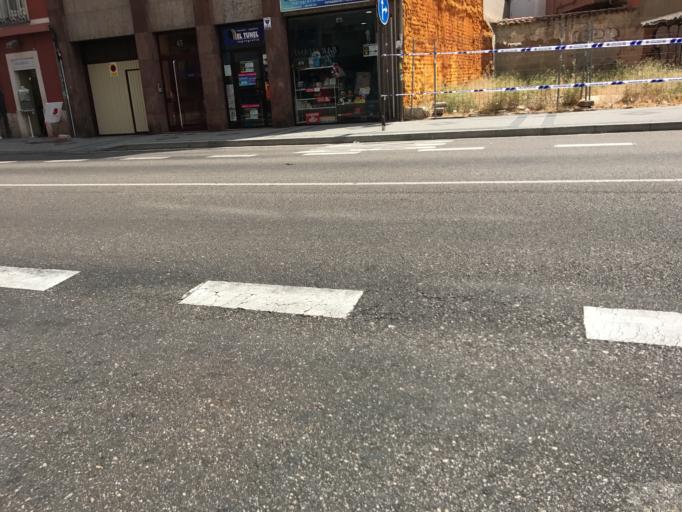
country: ES
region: Castille and Leon
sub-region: Provincia de Valladolid
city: Valladolid
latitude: 41.6453
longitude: -4.7209
